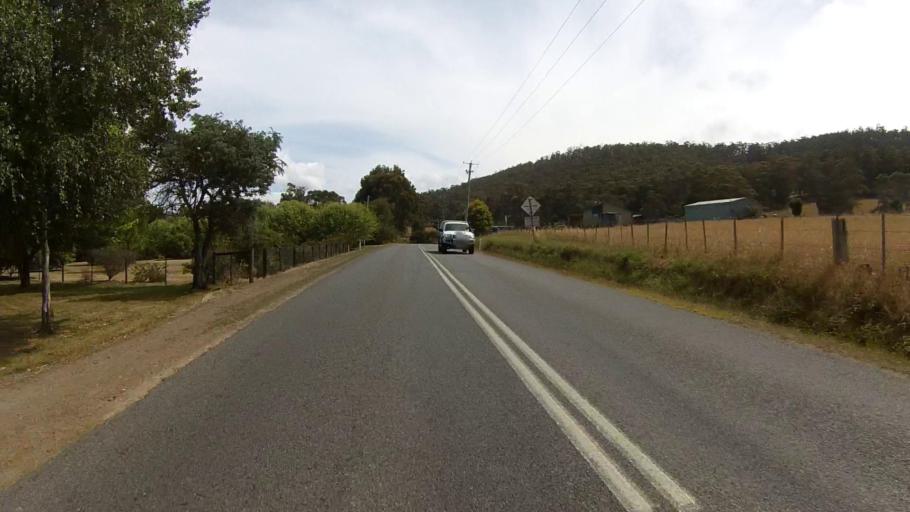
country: AU
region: Tasmania
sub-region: Huon Valley
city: Cygnet
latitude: -43.2089
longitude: 147.1156
